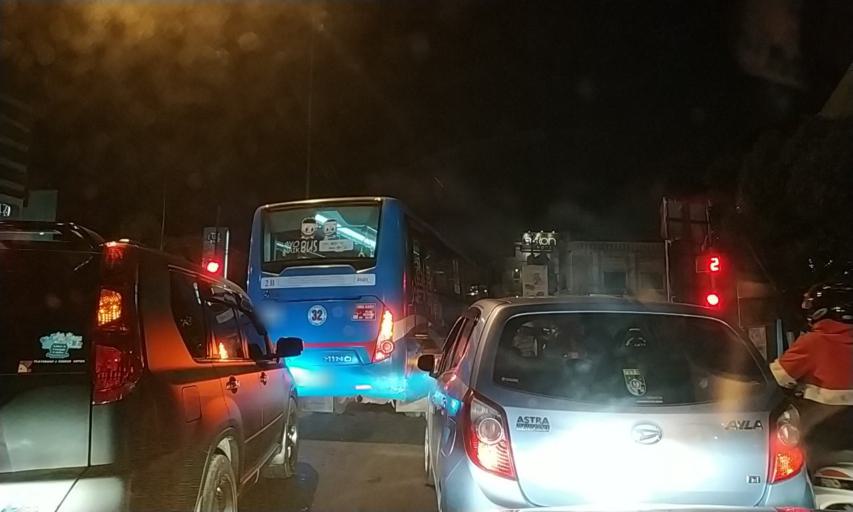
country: ID
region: Daerah Istimewa Yogyakarta
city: Yogyakarta
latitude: -7.7906
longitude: 110.3539
